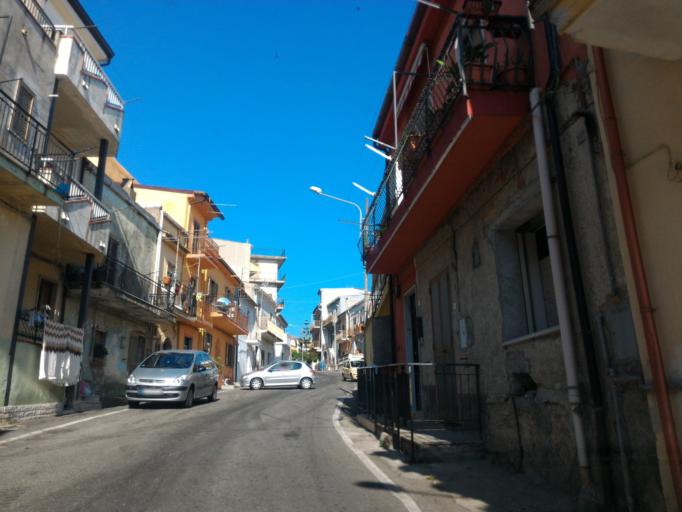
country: IT
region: Calabria
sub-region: Provincia di Crotone
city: Ciro
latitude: 39.3820
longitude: 17.0654
